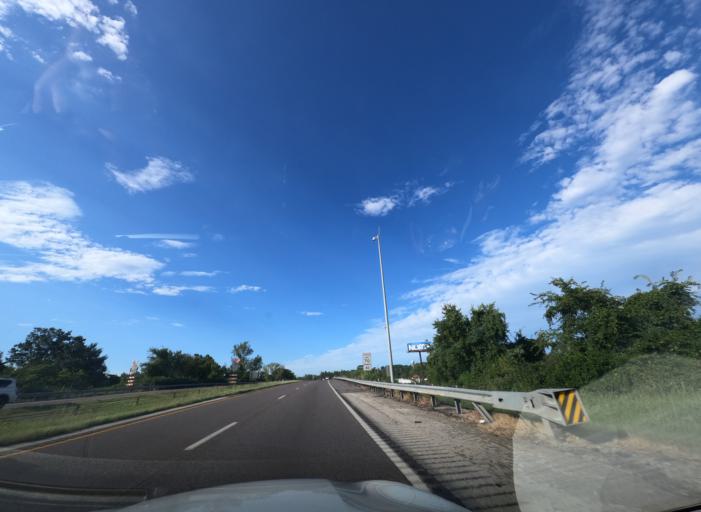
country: US
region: Missouri
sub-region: Jefferson County
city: Festus
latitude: 38.2233
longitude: -90.4059
